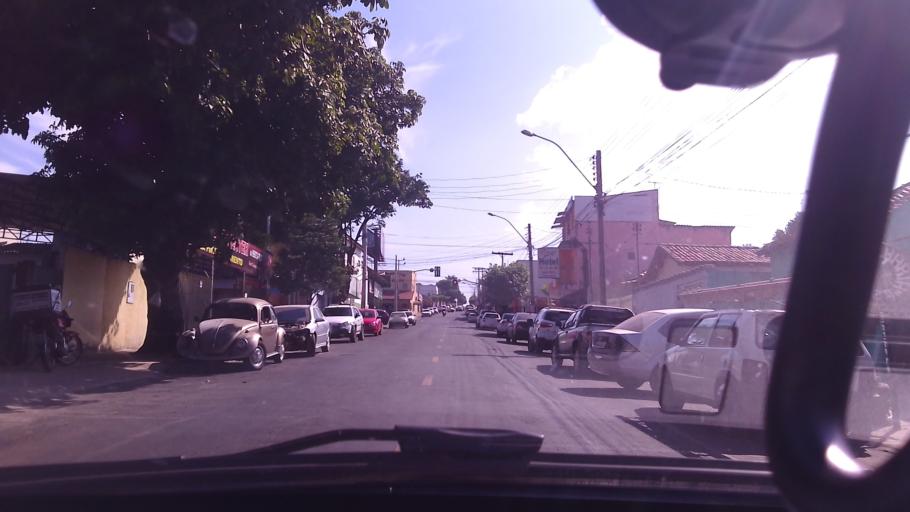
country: BR
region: Goias
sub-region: Mineiros
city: Mineiros
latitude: -17.5638
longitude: -52.5503
